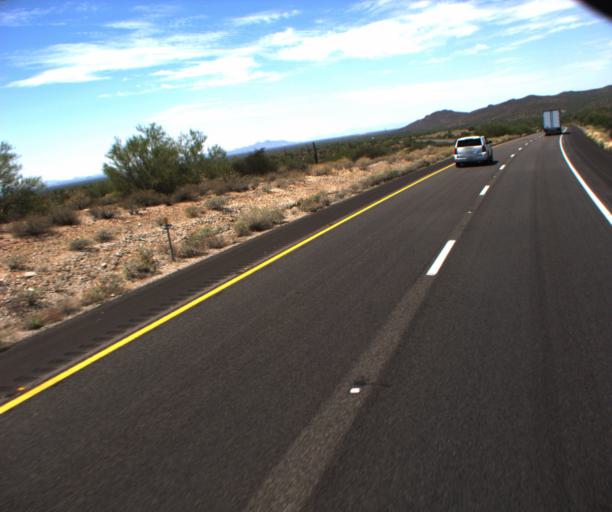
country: US
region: Arizona
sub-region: Pinal County
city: Gold Camp
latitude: 33.2631
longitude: -111.2666
